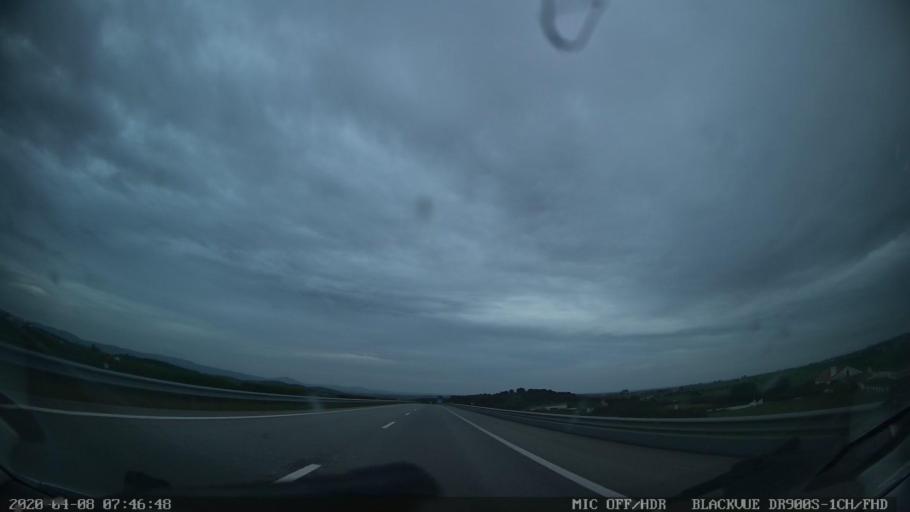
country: PT
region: Evora
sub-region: Estremoz
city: Estremoz
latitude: 38.8242
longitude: -7.5871
